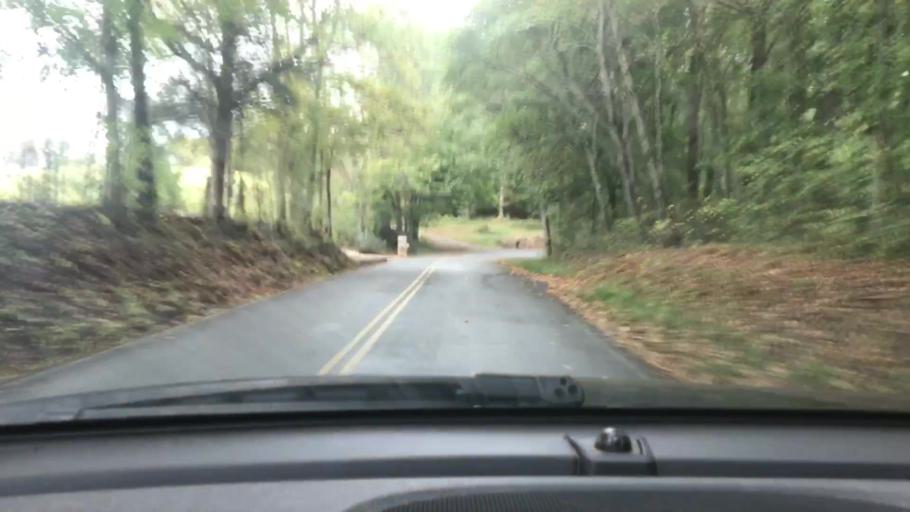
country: US
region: Tennessee
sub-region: Dickson County
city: Charlotte
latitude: 36.1902
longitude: -87.2851
